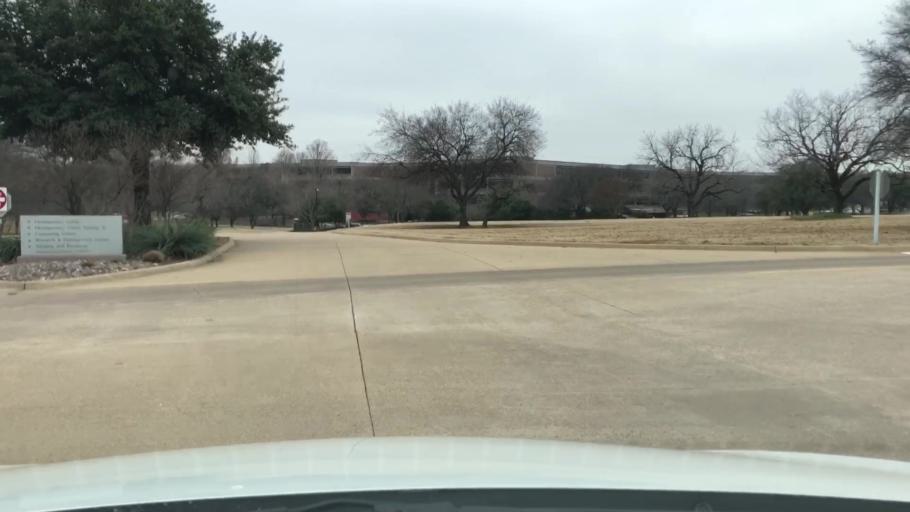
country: US
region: Texas
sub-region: Denton County
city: The Colony
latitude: 33.0796
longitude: -96.8432
